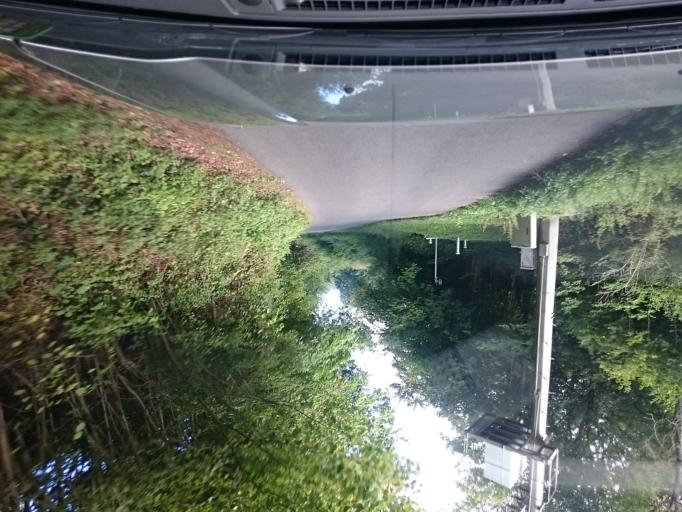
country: DE
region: Bavaria
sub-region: Upper Palatinate
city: Hirschbach
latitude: 49.5535
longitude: 11.5220
